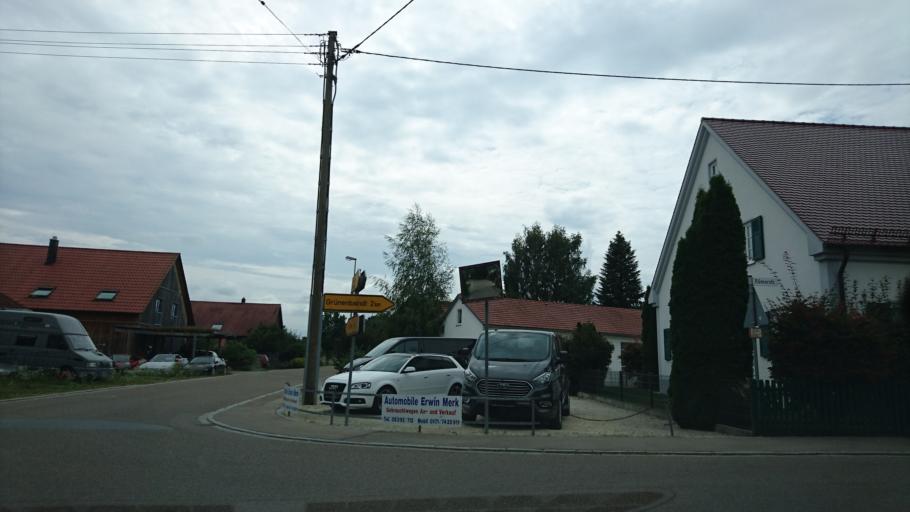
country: DE
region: Bavaria
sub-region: Swabia
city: Dinkelscherben
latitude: 48.3609
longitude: 10.5680
